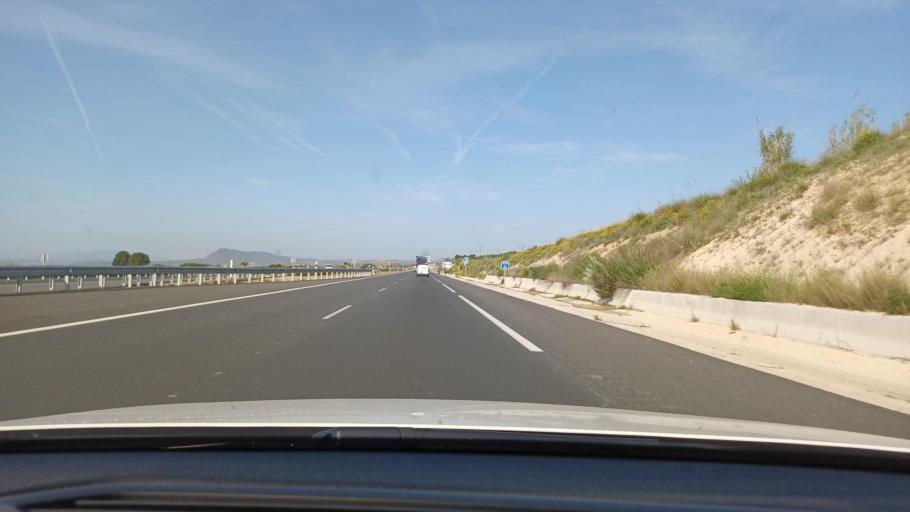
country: ES
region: Valencia
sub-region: Provincia de Valencia
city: La Font de la Figuera
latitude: 38.7520
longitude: -0.9080
